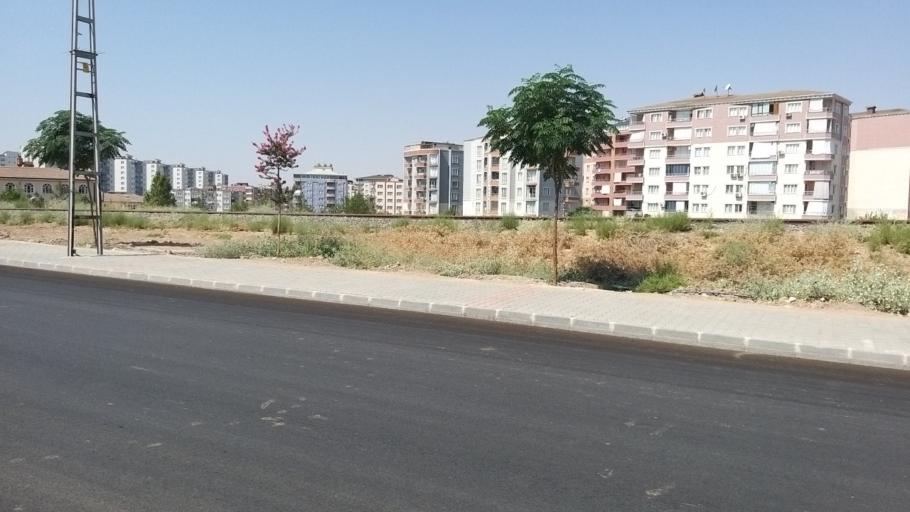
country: TR
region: Batman
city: Demiryol
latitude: 37.9082
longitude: 41.1449
